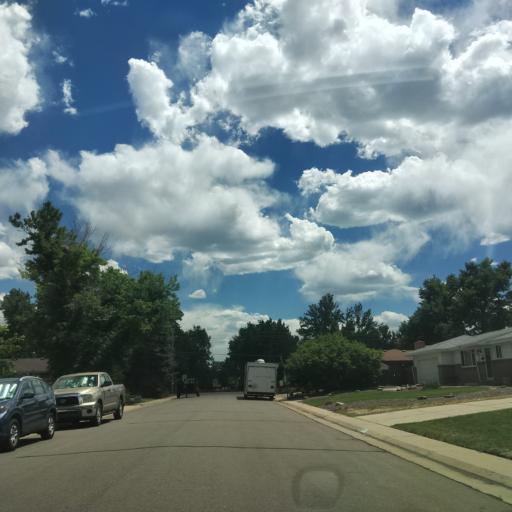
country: US
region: Colorado
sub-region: Jefferson County
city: Lakewood
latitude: 39.6865
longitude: -105.0984
